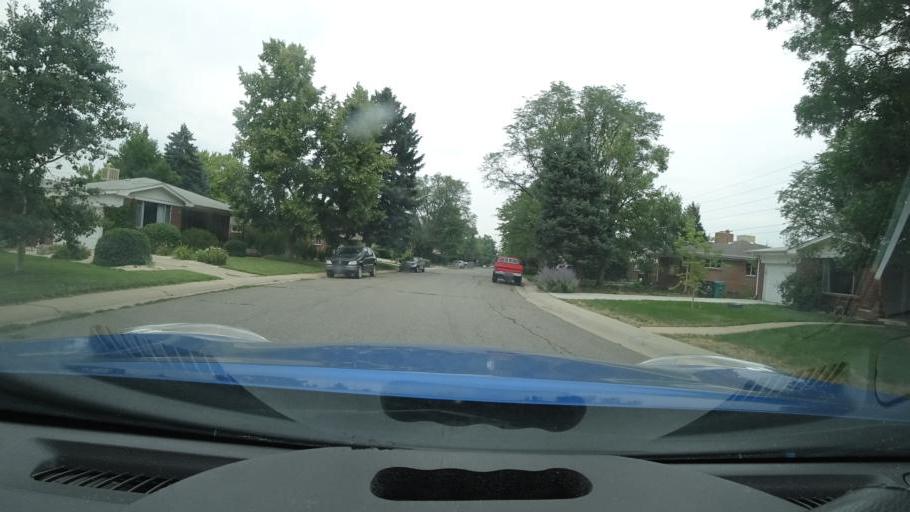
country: US
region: Colorado
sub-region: Arapahoe County
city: Glendale
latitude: 39.6881
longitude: -104.9183
